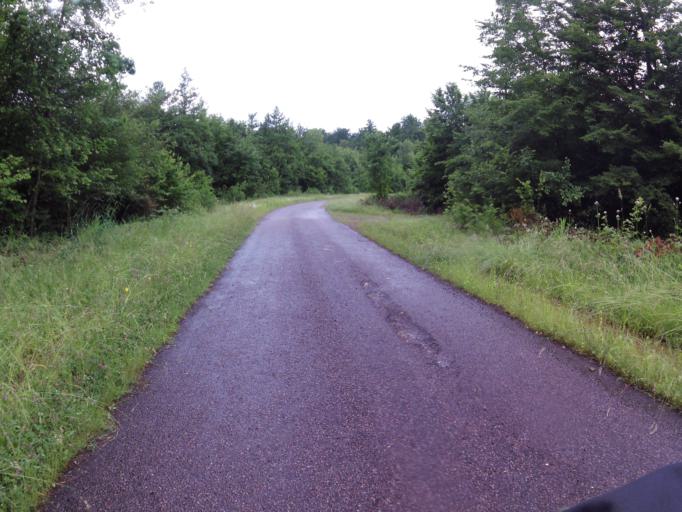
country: FR
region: Champagne-Ardenne
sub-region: Departement de la Marne
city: Sermaize-les-Bains
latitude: 48.7510
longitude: 4.9643
